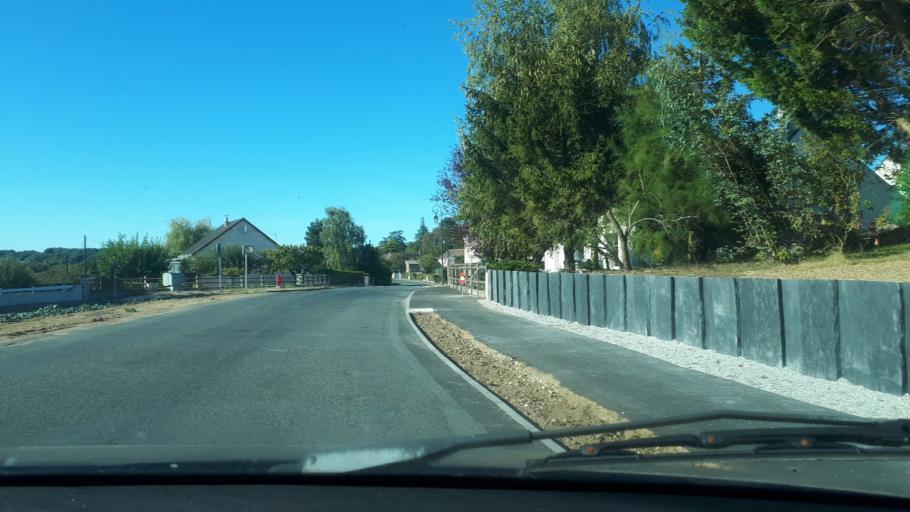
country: FR
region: Centre
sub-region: Departement du Loir-et-Cher
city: Villiers-sur-Loir
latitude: 47.8018
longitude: 1.0002
